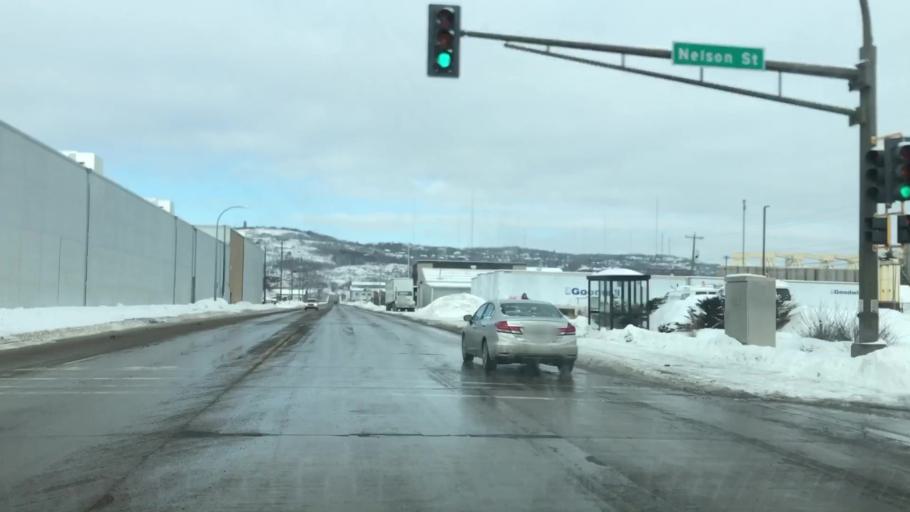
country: US
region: Minnesota
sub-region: Saint Louis County
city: Duluth
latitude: 46.7601
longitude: -92.1095
